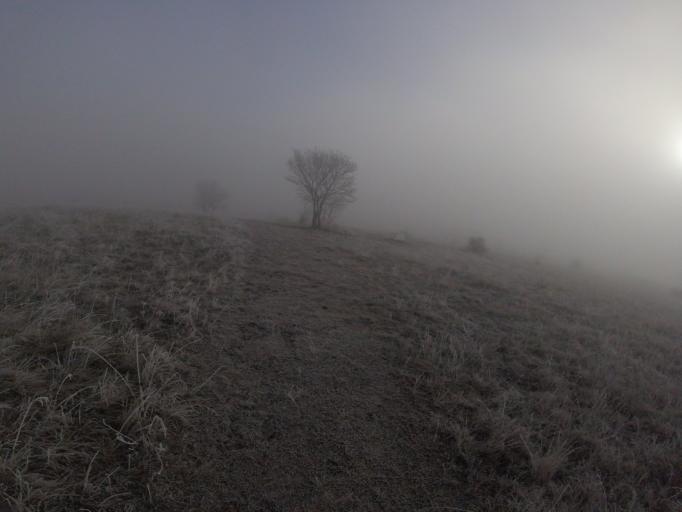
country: HU
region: Fejer
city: Csakvar
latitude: 47.3888
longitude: 18.4042
